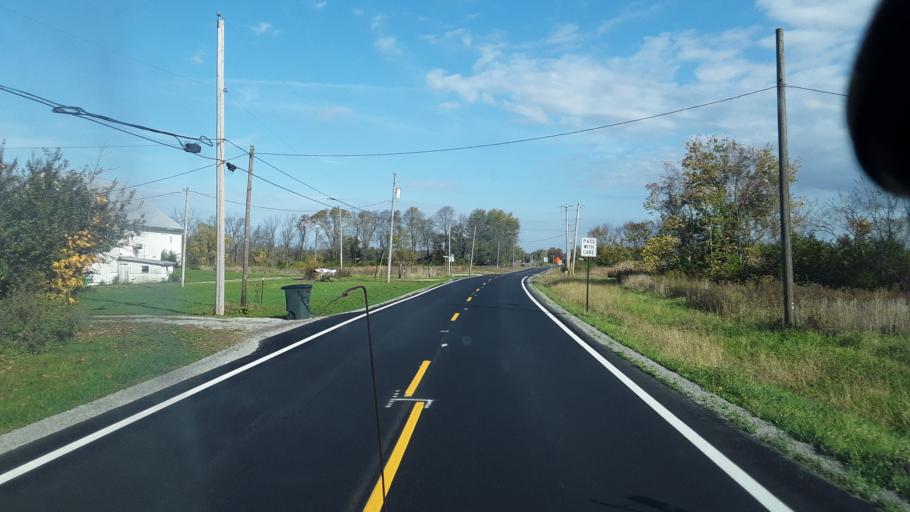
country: US
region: Ohio
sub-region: Highland County
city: Leesburg
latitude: 39.3165
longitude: -83.5875
